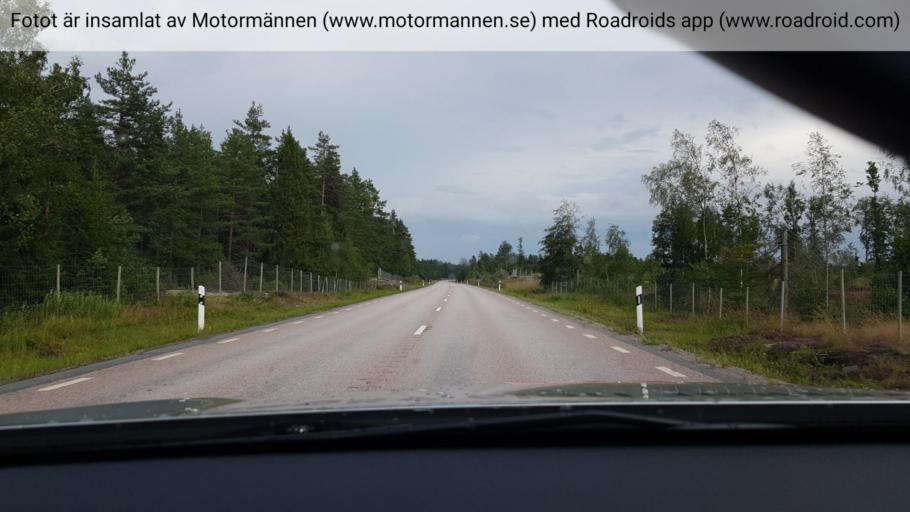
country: SE
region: Uppsala
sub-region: Osthammars Kommun
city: Osterbybruk
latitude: 60.3863
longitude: 17.9598
